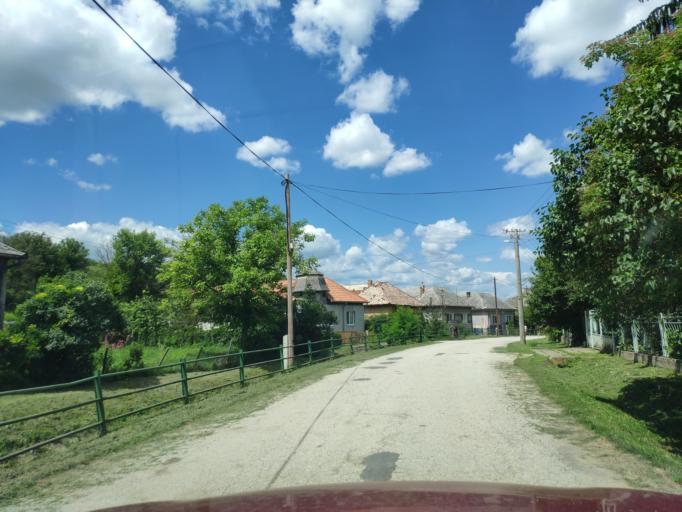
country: HU
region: Borsod-Abauj-Zemplen
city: Ozd
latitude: 48.2806
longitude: 20.2146
